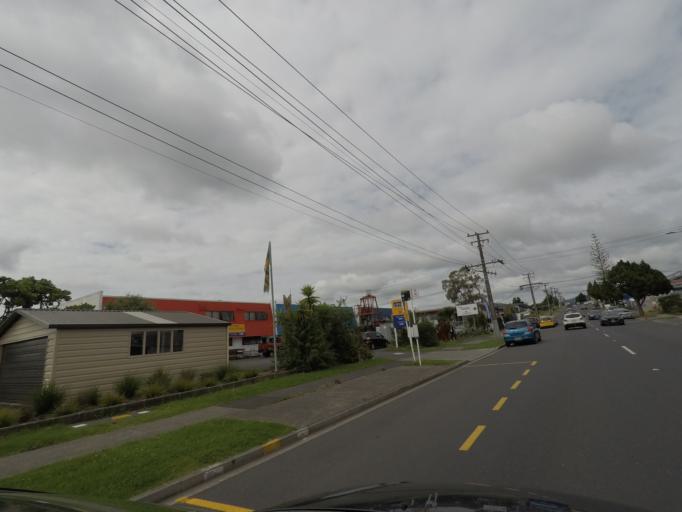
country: NZ
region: Auckland
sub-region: Auckland
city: Waitakere
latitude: -36.8917
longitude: 174.6306
